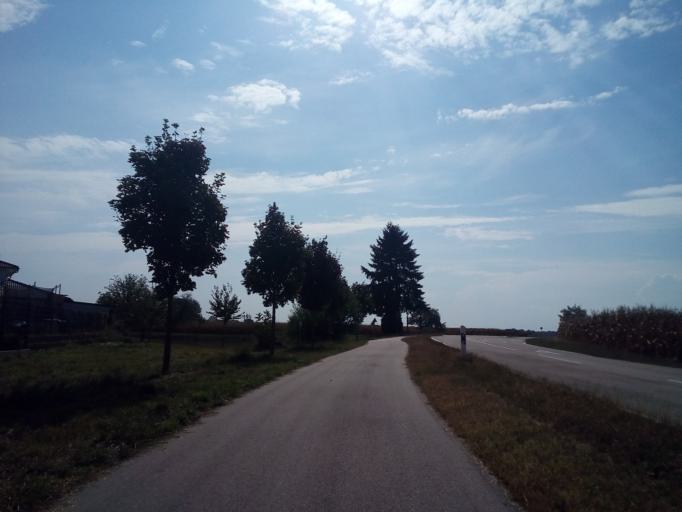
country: DE
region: Baden-Wuerttemberg
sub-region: Karlsruhe Region
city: Zell
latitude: 48.6860
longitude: 8.0509
